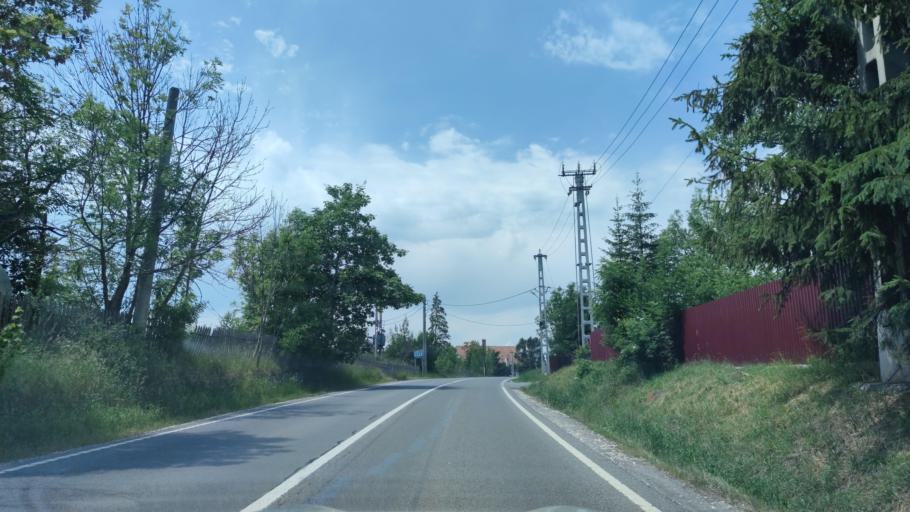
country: RO
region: Harghita
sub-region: Comuna Sandominic
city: Sandominic
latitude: 46.6237
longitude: 25.7189
